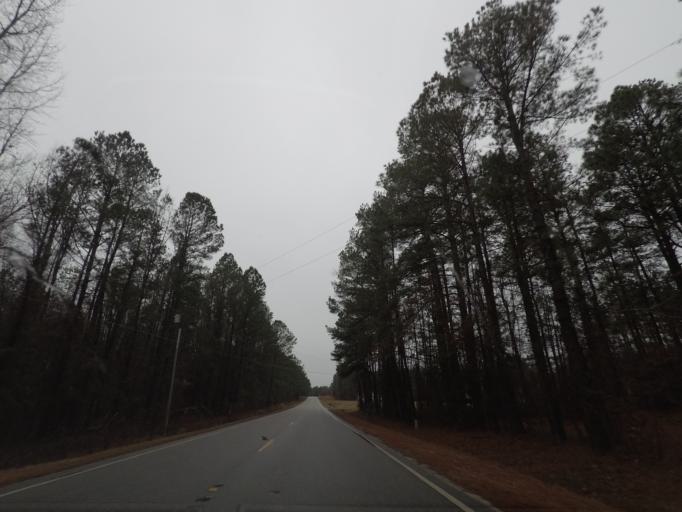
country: US
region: North Carolina
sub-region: Cumberland County
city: Spring Lake
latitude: 35.2831
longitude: -78.9853
